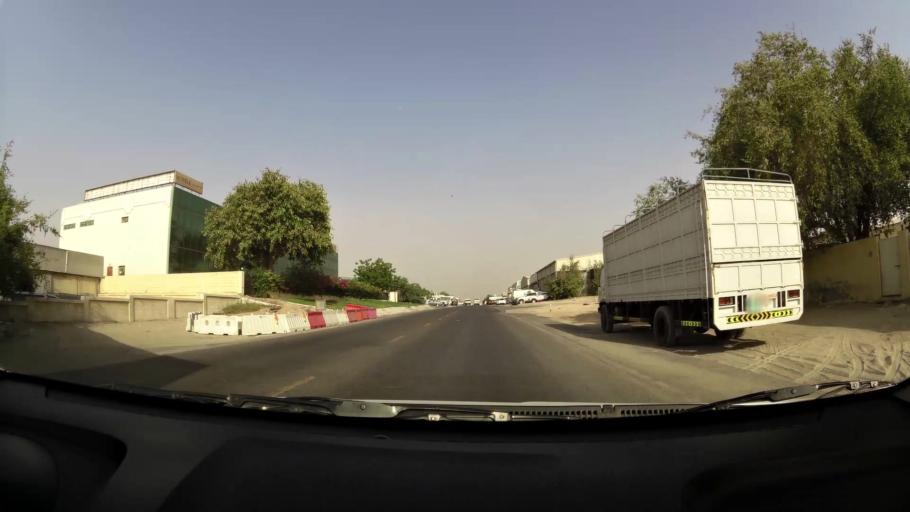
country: AE
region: Ash Shariqah
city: Sharjah
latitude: 25.2288
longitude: 55.3685
